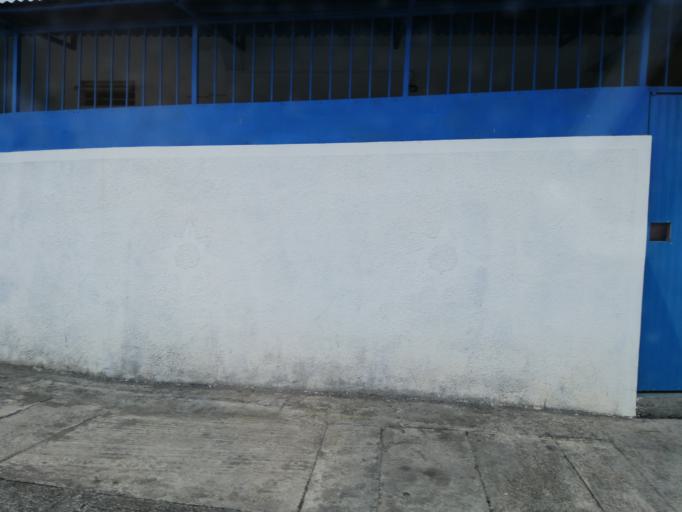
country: MU
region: Port Louis
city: Port Louis
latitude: -20.1620
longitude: 57.4814
